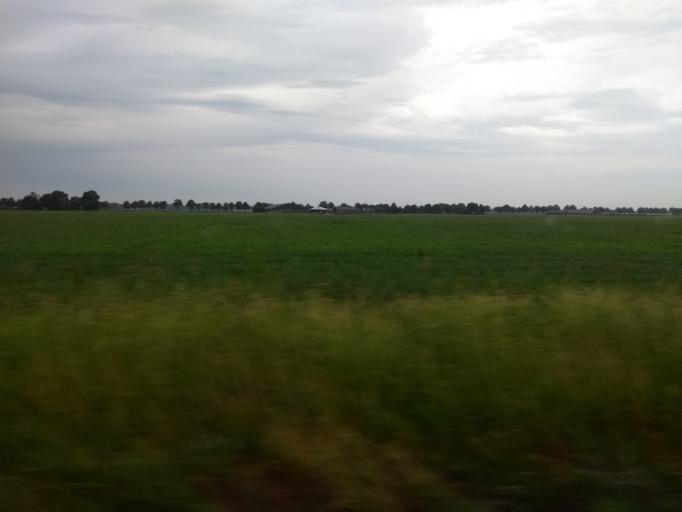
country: NL
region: Overijssel
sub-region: Gemeente Twenterand
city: Vroomshoop
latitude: 52.4917
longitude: 6.5937
